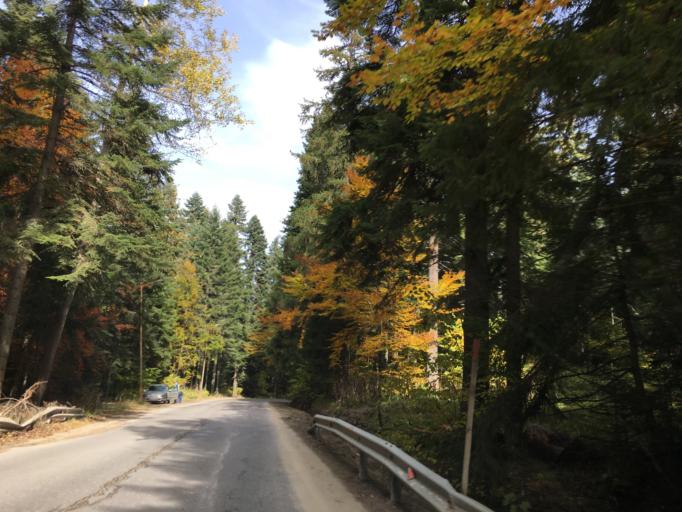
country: BG
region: Sofiya
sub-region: Obshtina Samokov
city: Samokov
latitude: 42.2690
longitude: 23.6117
